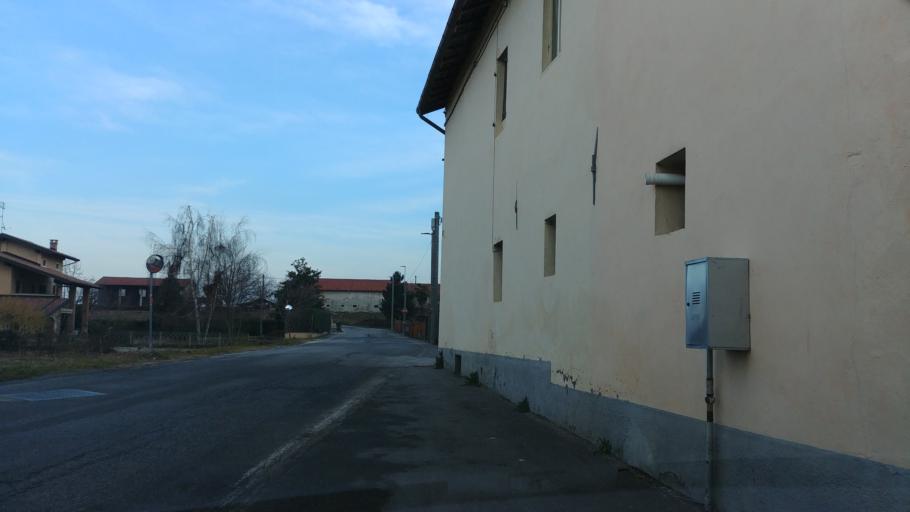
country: IT
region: Piedmont
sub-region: Provincia di Cuneo
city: Cuneo
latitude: 44.3980
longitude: 7.5770
